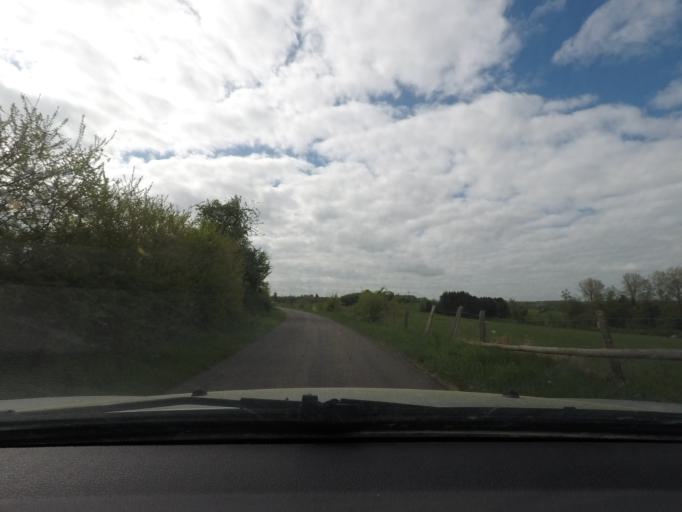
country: BE
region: Wallonia
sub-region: Province du Luxembourg
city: Habay-la-Vieille
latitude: 49.7120
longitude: 5.5979
